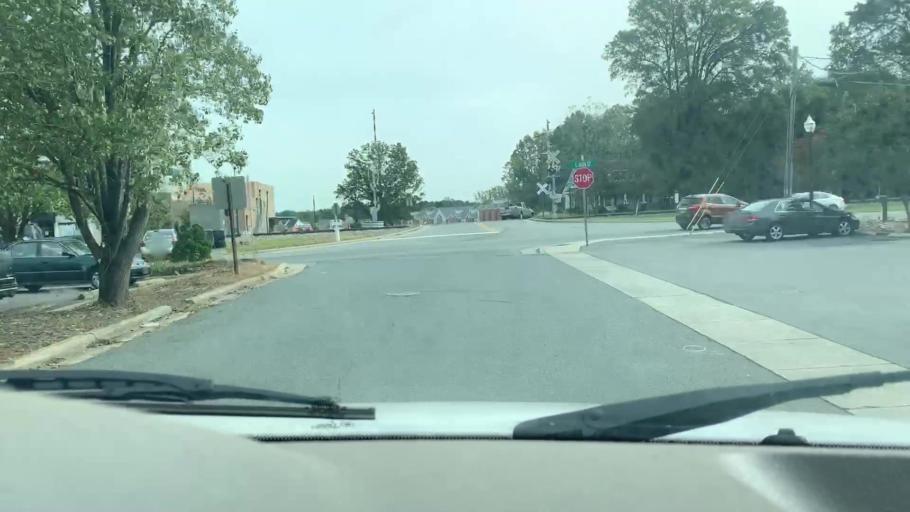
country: US
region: North Carolina
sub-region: Mecklenburg County
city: Cornelius
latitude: 35.4788
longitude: -80.8569
